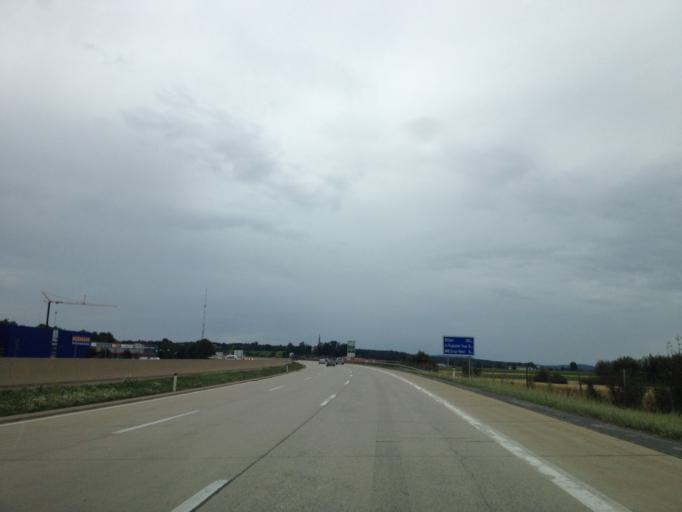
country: AT
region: Styria
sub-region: Politischer Bezirk Deutschlandsberg
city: Lannach
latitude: 46.9547
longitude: 15.3578
